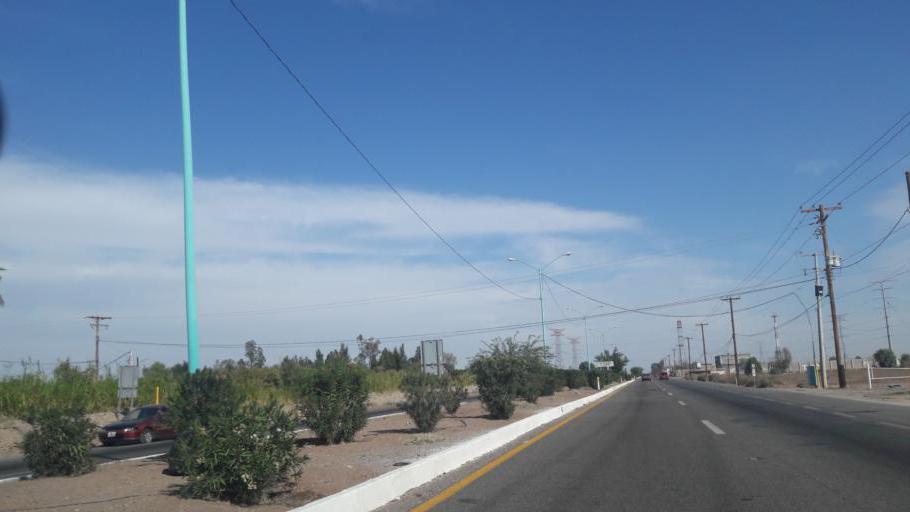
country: MX
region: Baja California
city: Progreso
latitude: 32.5893
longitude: -115.5621
